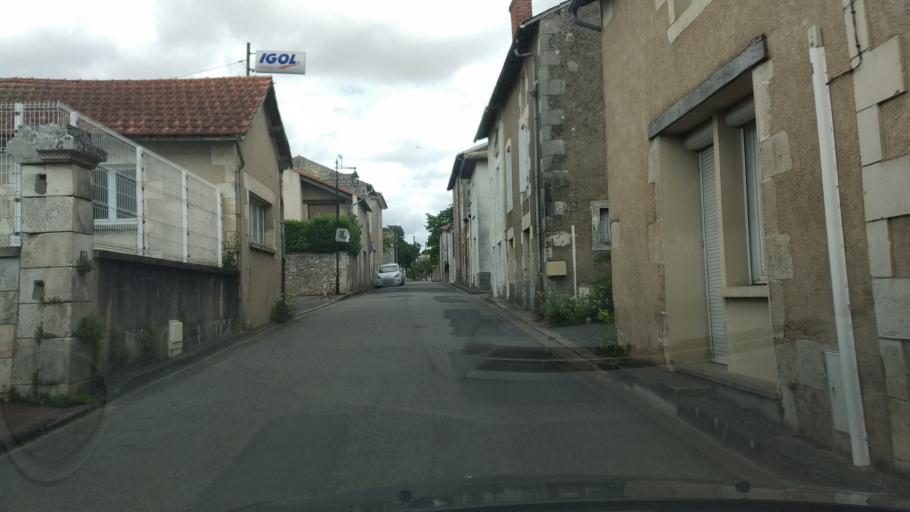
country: FR
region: Poitou-Charentes
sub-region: Departement de la Vienne
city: Vouille
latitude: 46.6415
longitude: 0.1668
